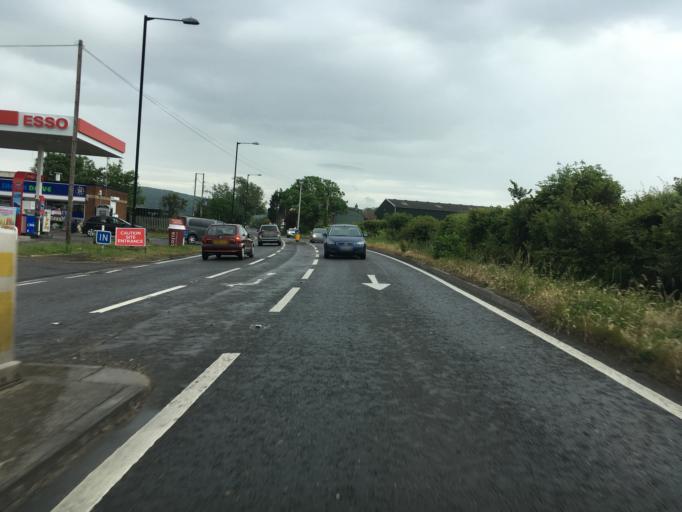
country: GB
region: England
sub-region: North Somerset
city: Congresbury
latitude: 51.3719
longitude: -2.8235
